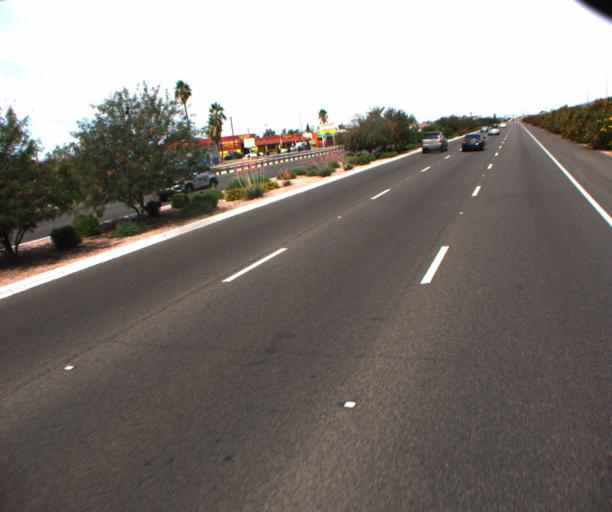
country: US
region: Arizona
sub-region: Maricopa County
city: El Mirage
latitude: 33.6124
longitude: -112.3163
